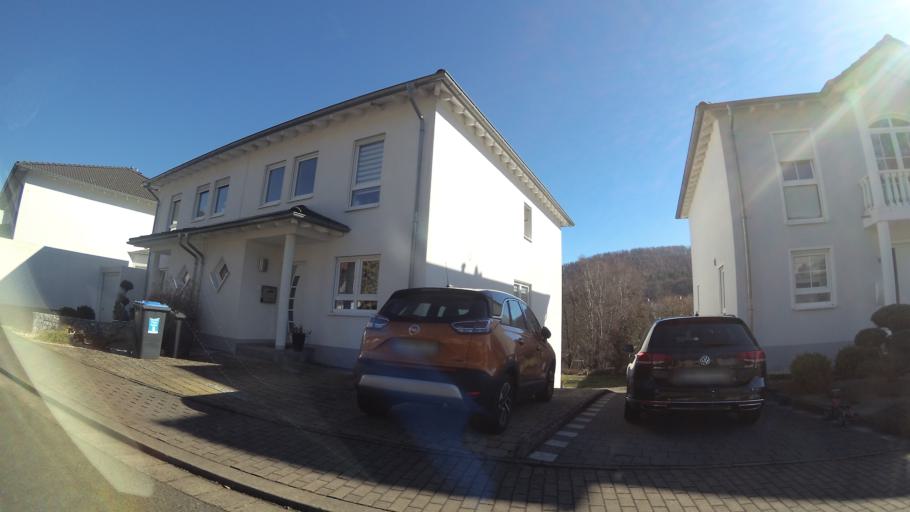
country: DE
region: Saarland
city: Sankt Ingbert
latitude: 49.2630
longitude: 7.0788
